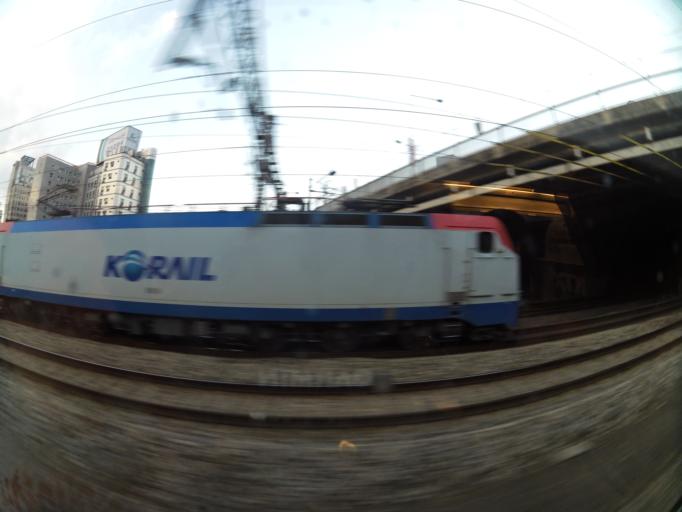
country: KR
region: Gyeonggi-do
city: Kwangmyong
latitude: 37.5172
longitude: 126.9162
